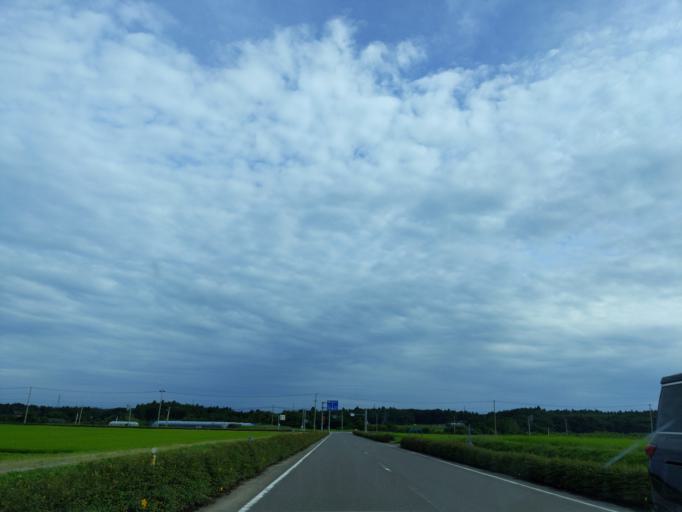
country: JP
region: Fukushima
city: Sukagawa
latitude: 37.3333
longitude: 140.3146
